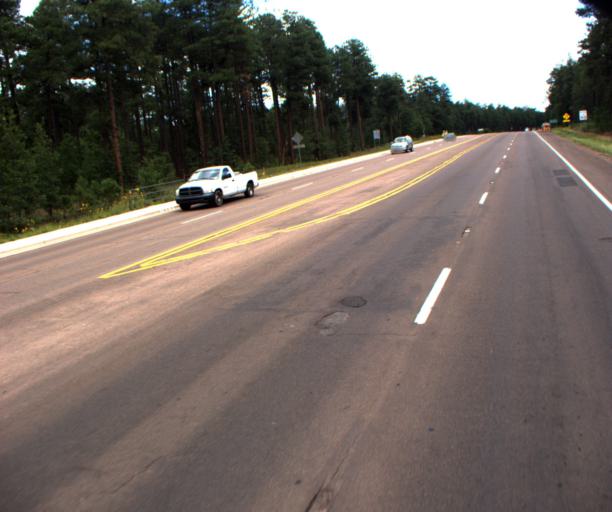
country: US
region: Arizona
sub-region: Navajo County
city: Pinetop-Lakeside
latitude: 34.1237
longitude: -109.9245
